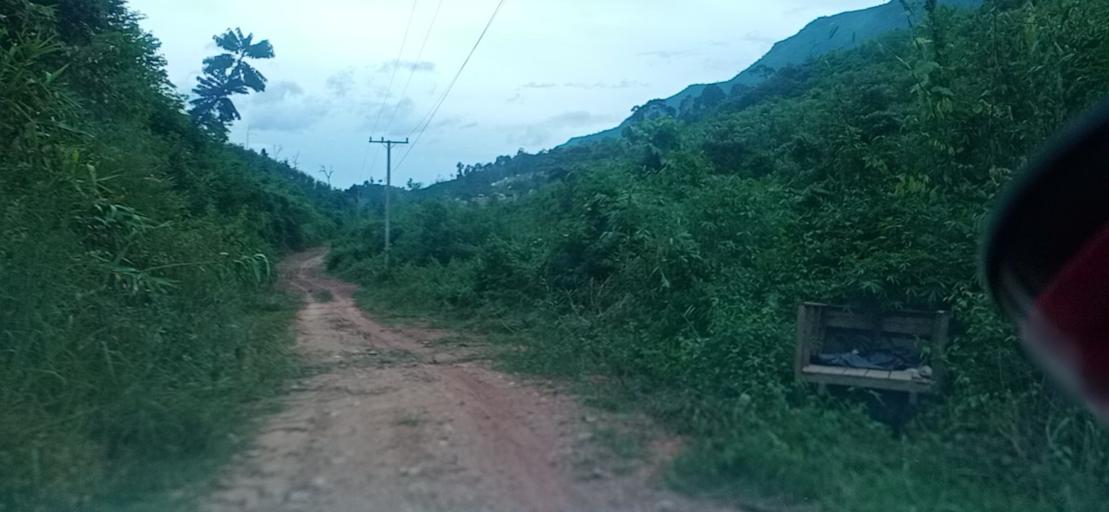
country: TH
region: Changwat Bueng Kan
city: Pak Khat
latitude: 18.5594
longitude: 103.2436
